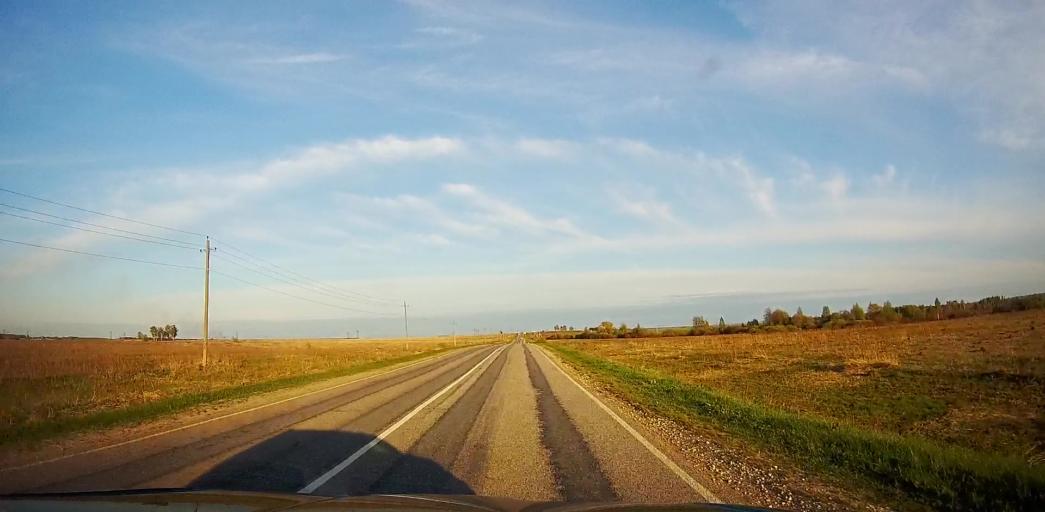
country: RU
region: Moskovskaya
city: Meshcherino
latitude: 55.2727
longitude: 38.2339
